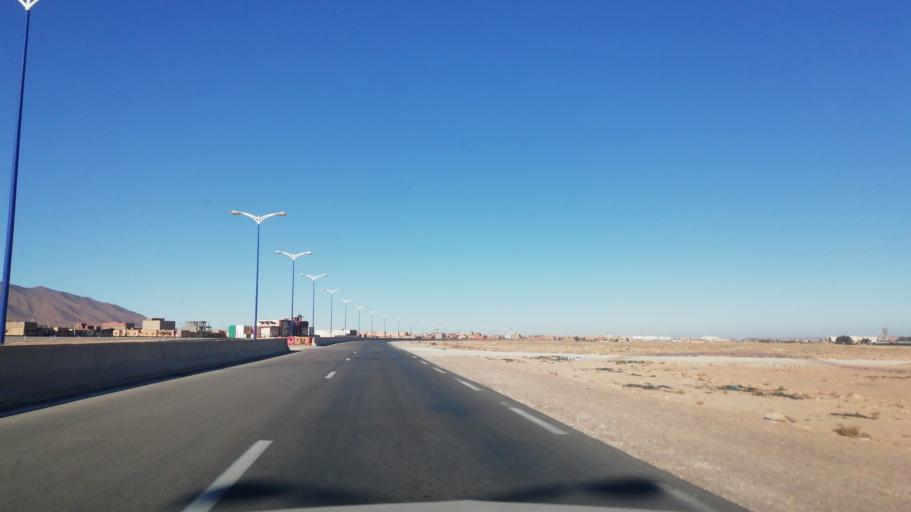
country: DZ
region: Wilaya de Naama
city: Naama
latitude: 33.5268
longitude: -0.2736
